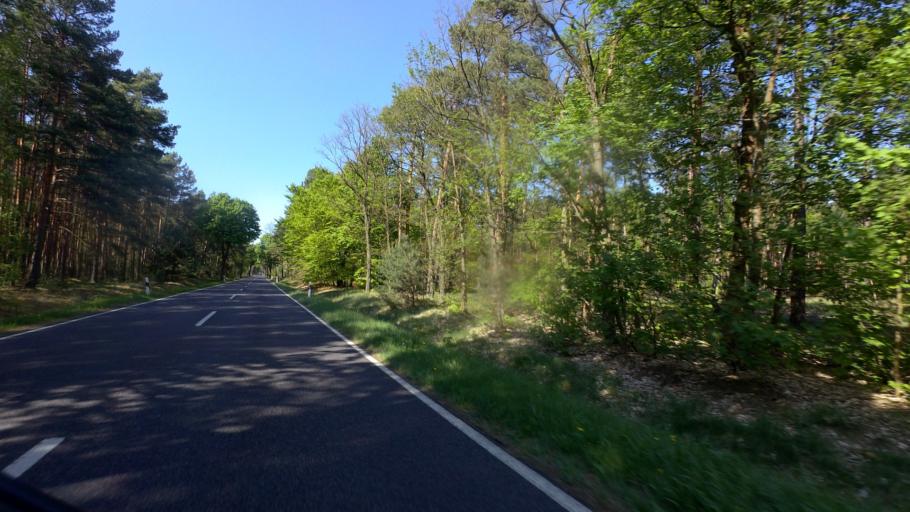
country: DE
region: Brandenburg
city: Halbe
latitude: 52.1360
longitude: 13.7507
